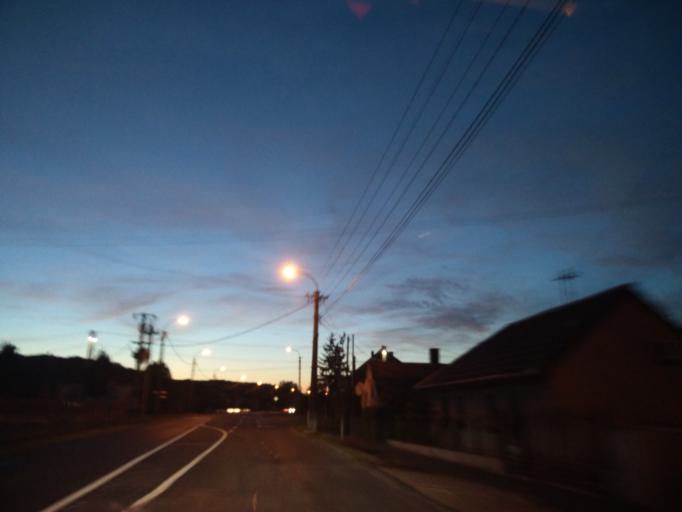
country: HU
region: Zala
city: Zalaegerszeg
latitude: 46.9393
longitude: 16.8508
